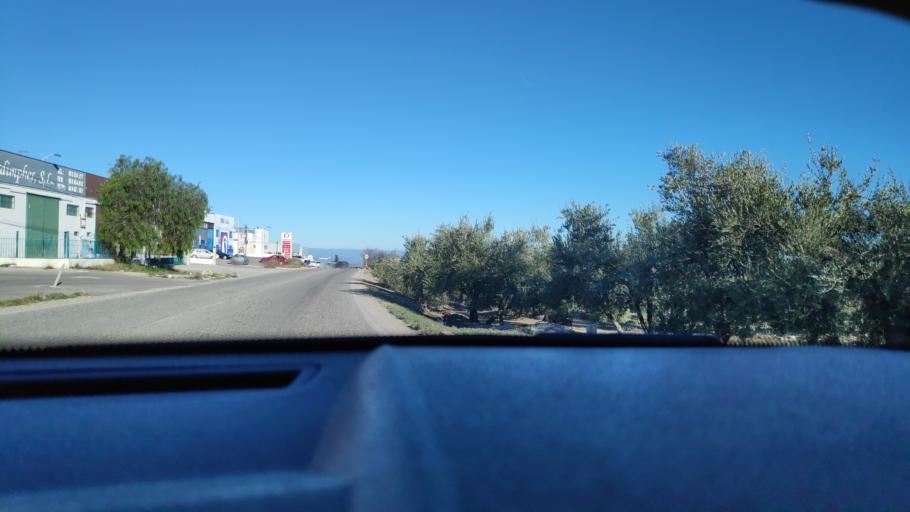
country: ES
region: Andalusia
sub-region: Provincia de Jaen
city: Mancha Real
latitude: 37.7980
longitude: -3.6087
